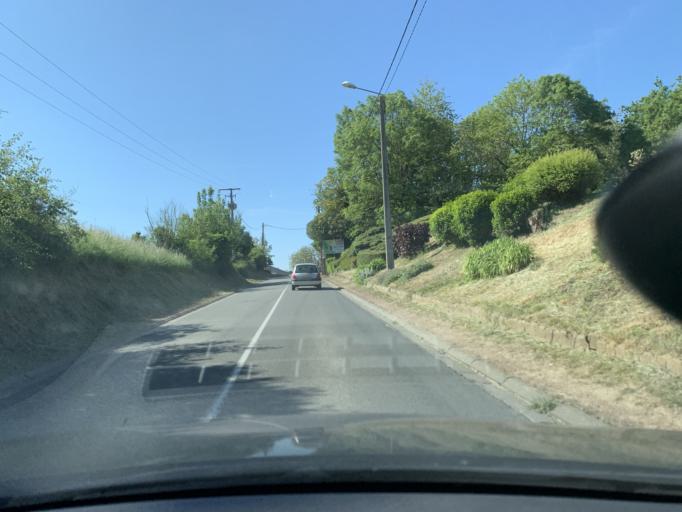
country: FR
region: Nord-Pas-de-Calais
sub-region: Departement du Nord
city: Rumilly-en-Cambresis
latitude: 50.1002
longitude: 3.2444
